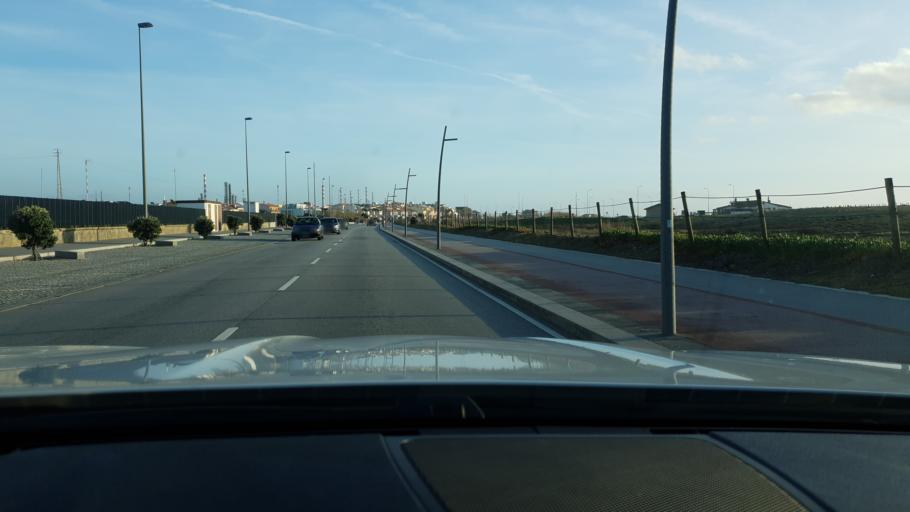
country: PT
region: Porto
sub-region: Matosinhos
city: Lavra
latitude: 41.2333
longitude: -8.7205
